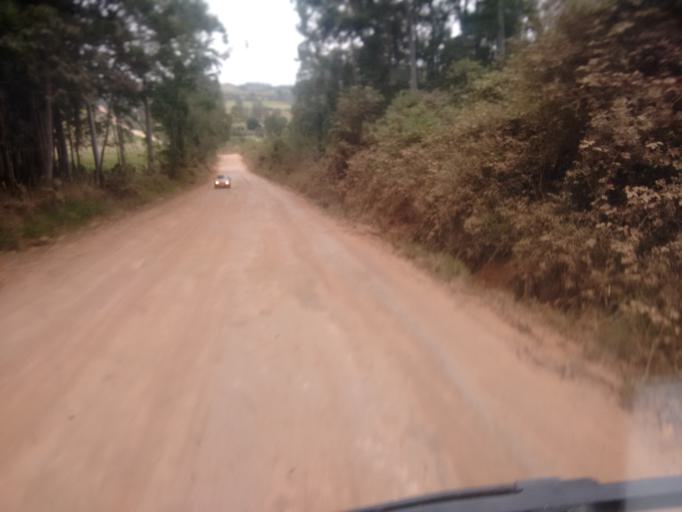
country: BR
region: Rio Grande do Sul
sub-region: Camaqua
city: Camaqua
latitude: -30.8077
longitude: -51.8274
